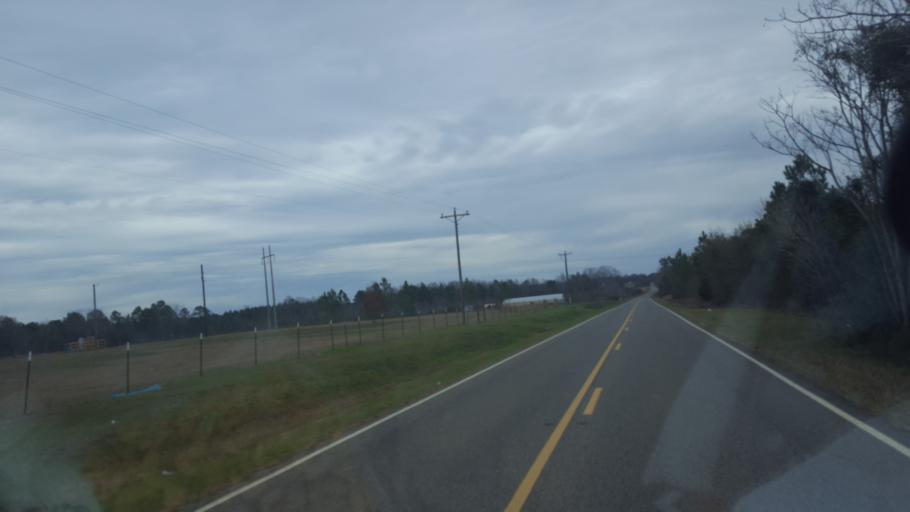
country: US
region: Georgia
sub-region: Ben Hill County
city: Fitzgerald
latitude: 31.7438
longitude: -83.3074
